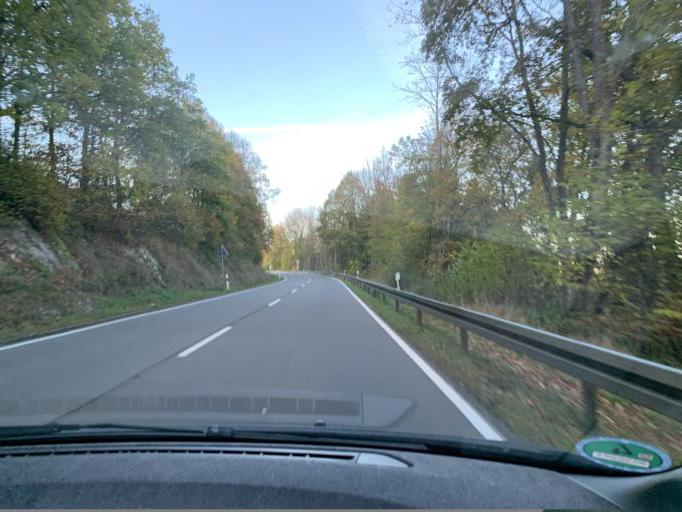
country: DE
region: North Rhine-Westphalia
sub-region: Regierungsbezirk Koln
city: Simmerath
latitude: 50.5861
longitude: 6.3733
